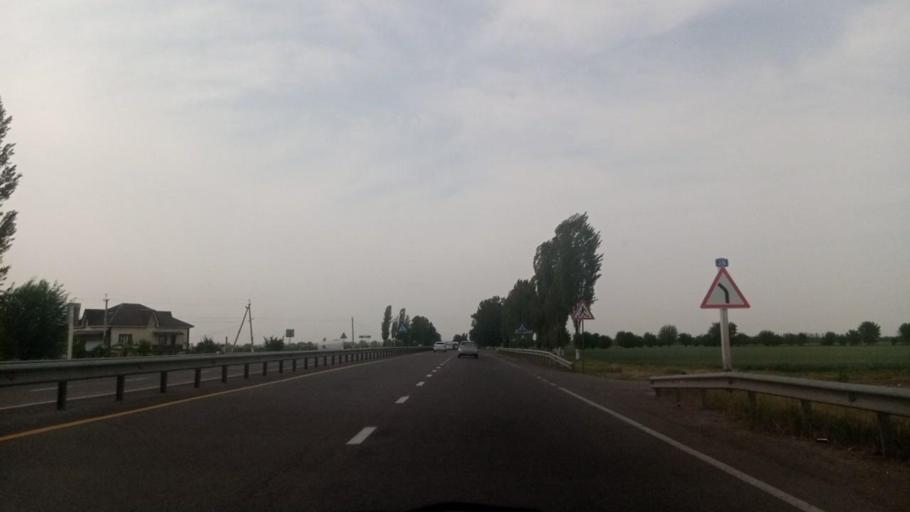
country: UZ
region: Toshkent Shahri
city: Bektemir
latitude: 41.1363
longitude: 69.4343
